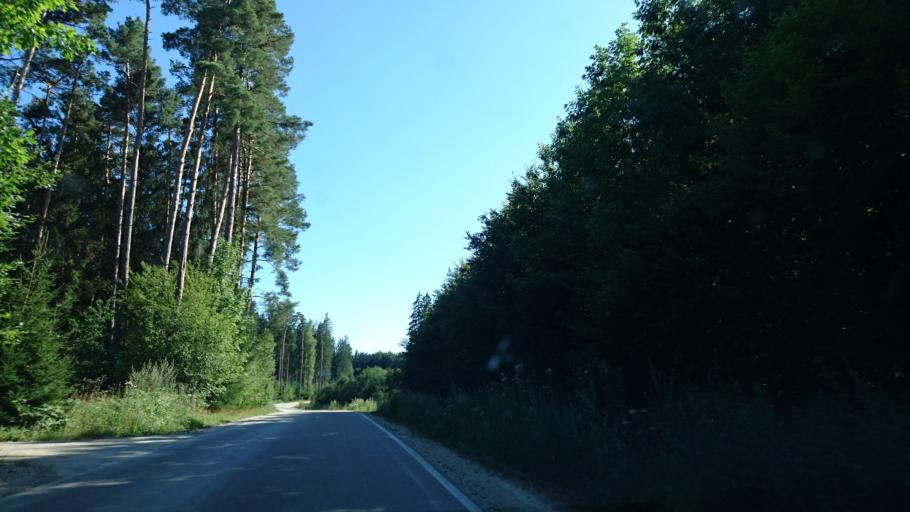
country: DE
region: Bavaria
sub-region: Swabia
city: Gablingen
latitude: 48.4529
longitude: 10.7740
